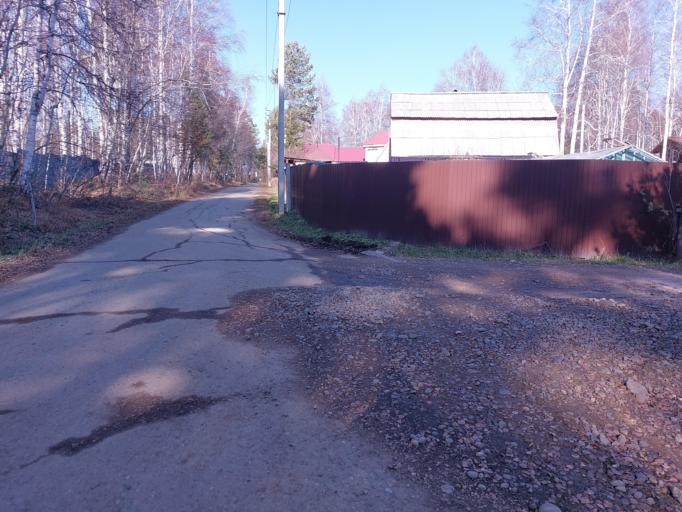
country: RU
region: Irkutsk
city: Pivovarikha
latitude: 52.1874
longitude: 104.4617
